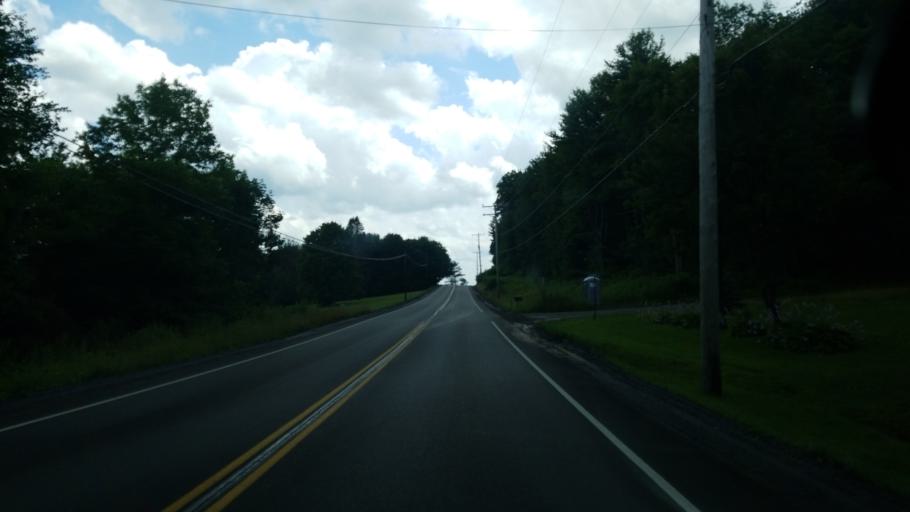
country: US
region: Pennsylvania
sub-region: Jefferson County
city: Brookville
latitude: 41.2352
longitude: -79.1112
